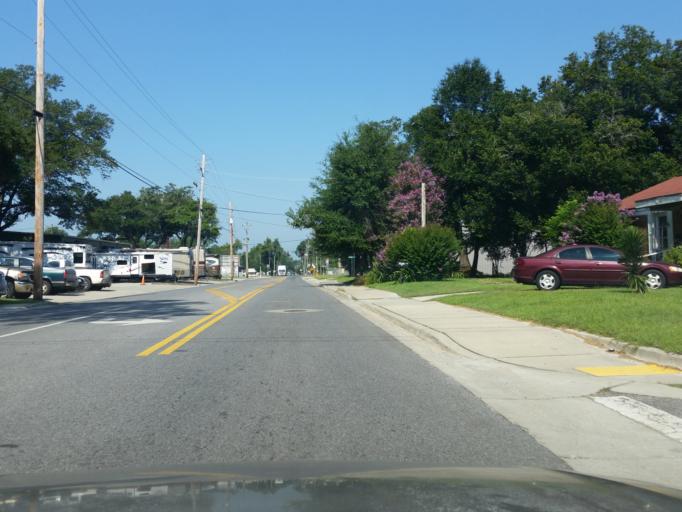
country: US
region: Florida
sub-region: Escambia County
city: Ensley
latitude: 30.5187
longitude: -87.2706
